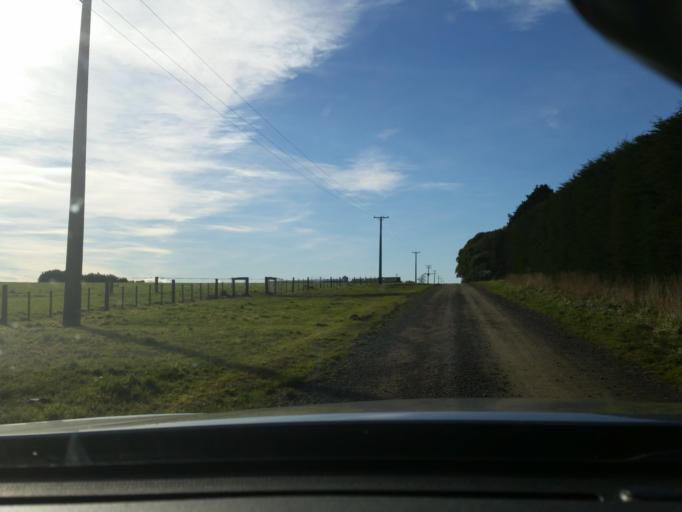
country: NZ
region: Southland
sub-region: Southland District
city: Riverton
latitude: -46.2864
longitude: 168.0474
